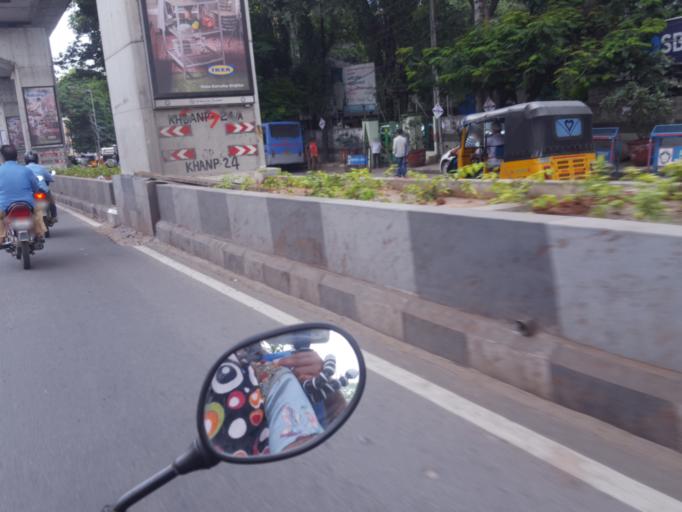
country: IN
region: Telangana
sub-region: Hyderabad
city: Hyderabad
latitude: 17.4059
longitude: 78.4632
